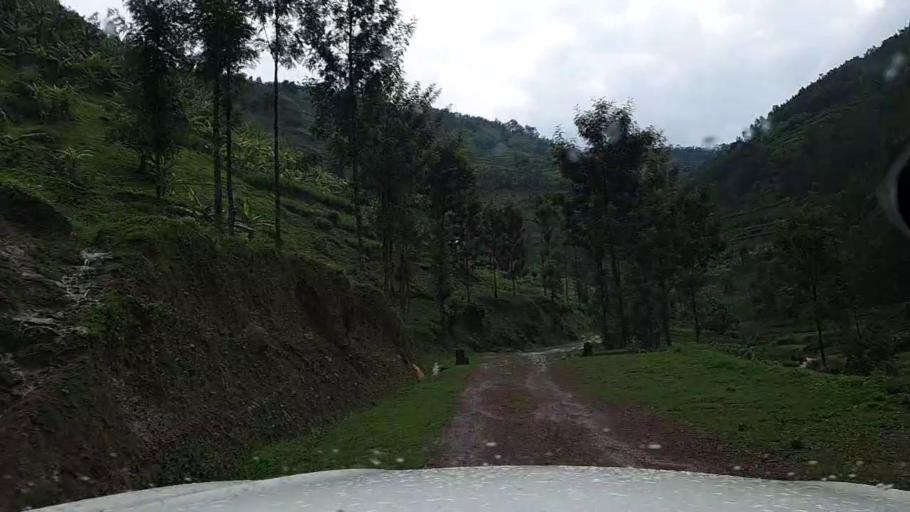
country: RW
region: Northern Province
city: Byumba
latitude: -1.7224
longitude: 29.9119
